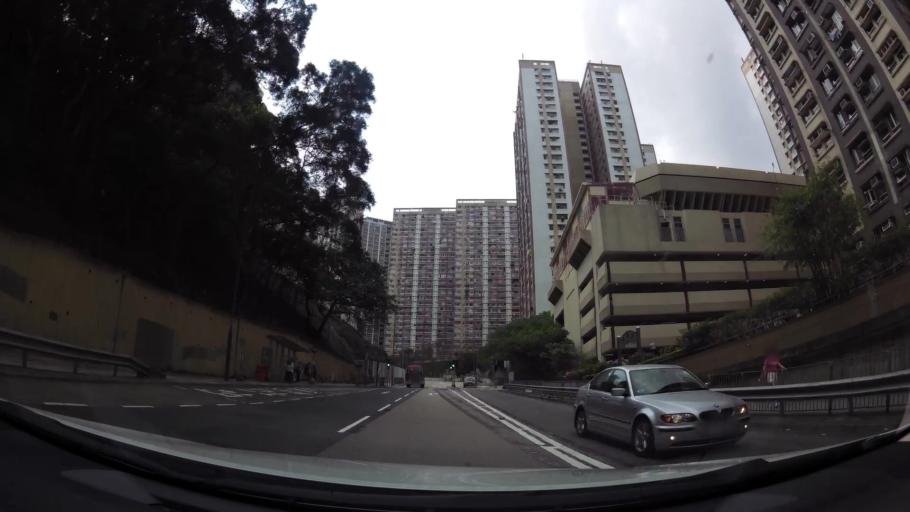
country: HK
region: Kowloon City
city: Kowloon
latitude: 22.3230
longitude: 114.2209
